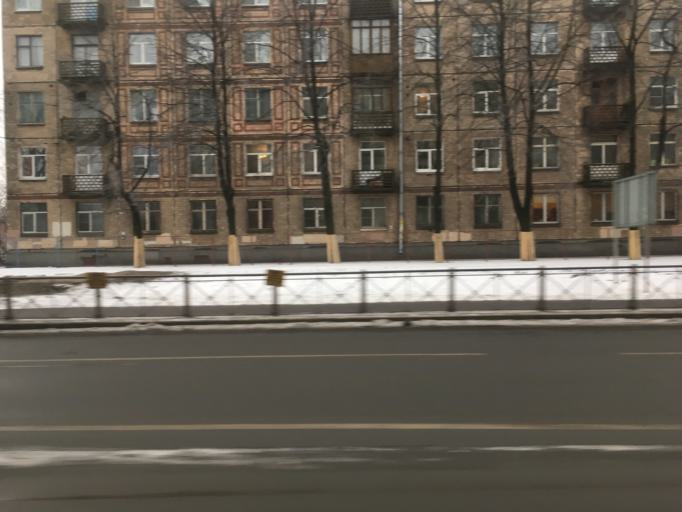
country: RU
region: St.-Petersburg
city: Obukhovo
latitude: 59.8717
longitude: 30.4392
